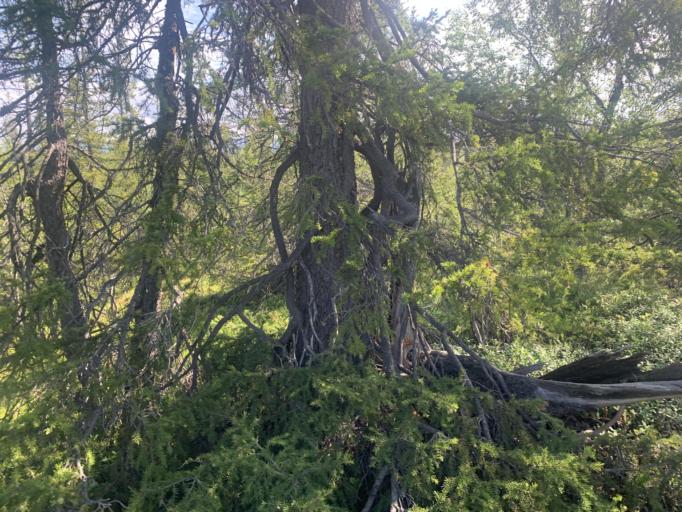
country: RU
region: Murmansk
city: Monchegorsk
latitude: 67.7356
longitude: 33.0701
